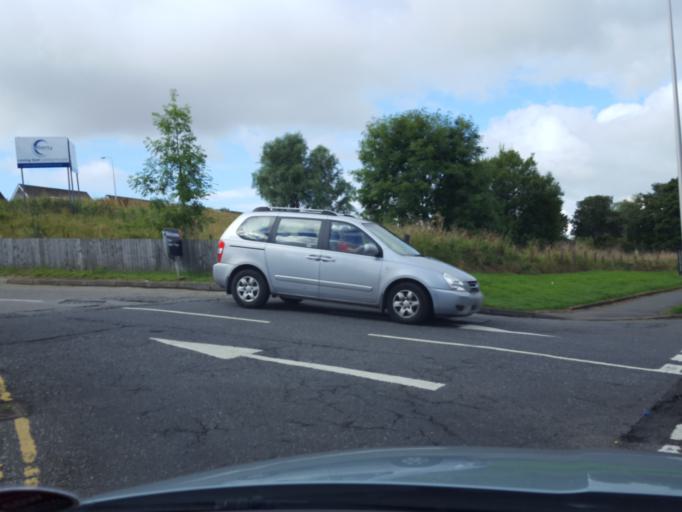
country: GB
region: Scotland
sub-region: Fife
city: Townhill
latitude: 56.0606
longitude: -3.4252
